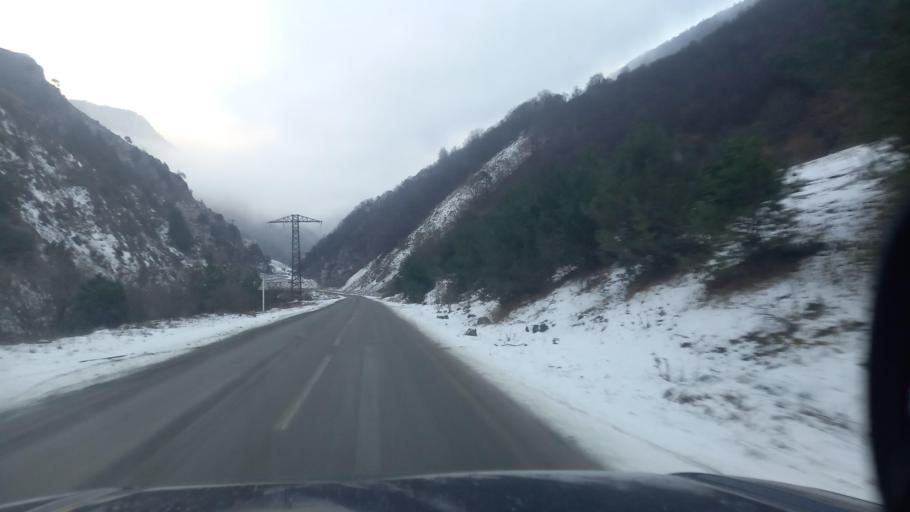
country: RU
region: Ingushetiya
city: Dzhayrakh
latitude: 42.7910
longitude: 44.7688
